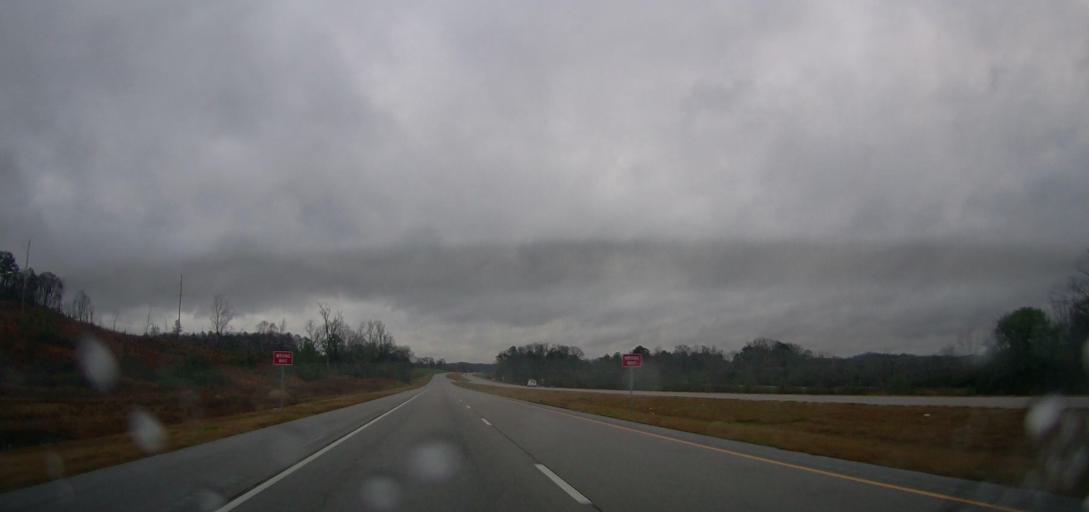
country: US
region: Alabama
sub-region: Bibb County
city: Centreville
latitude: 32.9415
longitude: -87.0754
